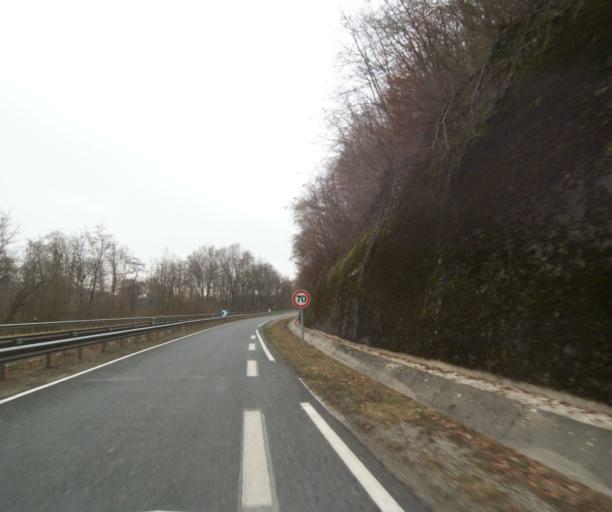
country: FR
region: Champagne-Ardenne
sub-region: Departement de la Haute-Marne
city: Chevillon
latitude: 48.5396
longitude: 5.0981
